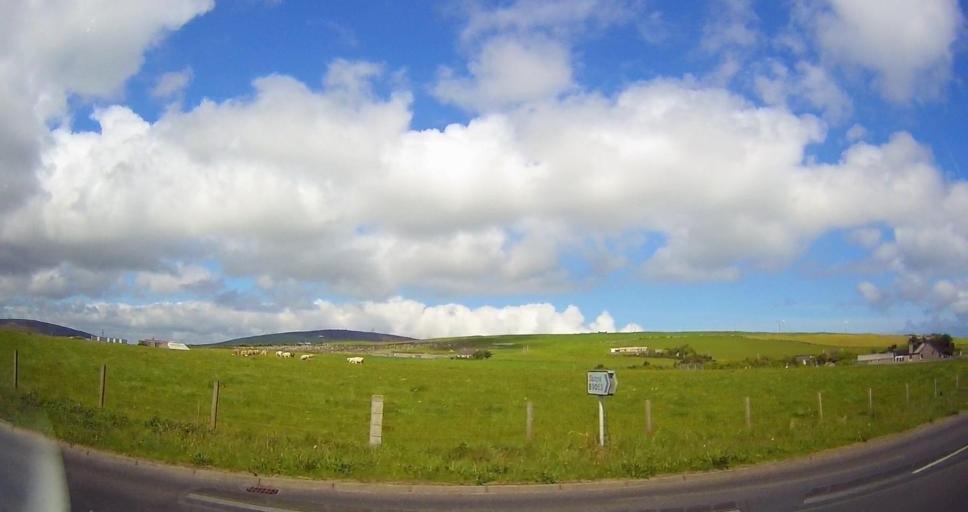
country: GB
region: Scotland
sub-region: Orkney Islands
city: Orkney
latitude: 58.9661
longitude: -2.9769
